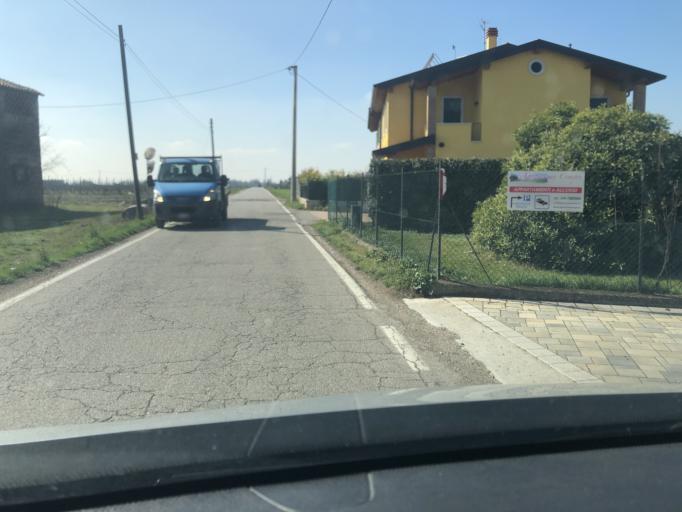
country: IT
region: Veneto
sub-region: Provincia di Verona
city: Villafranca di Verona
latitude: 45.3804
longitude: 10.8414
